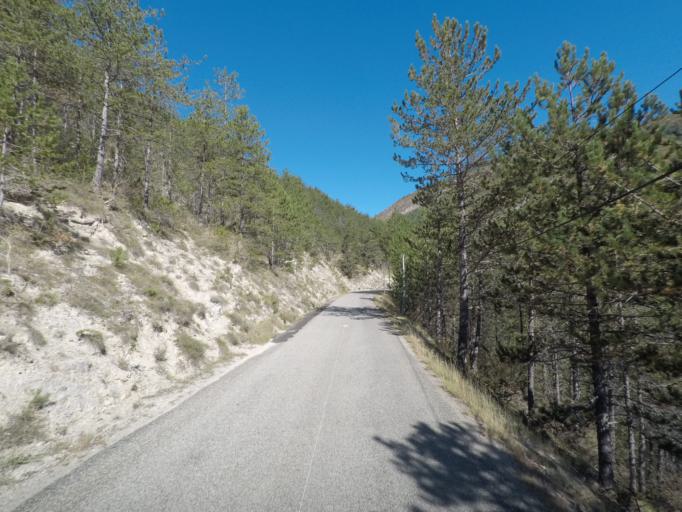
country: FR
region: Rhone-Alpes
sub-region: Departement de la Drome
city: Die
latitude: 44.6698
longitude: 5.2694
